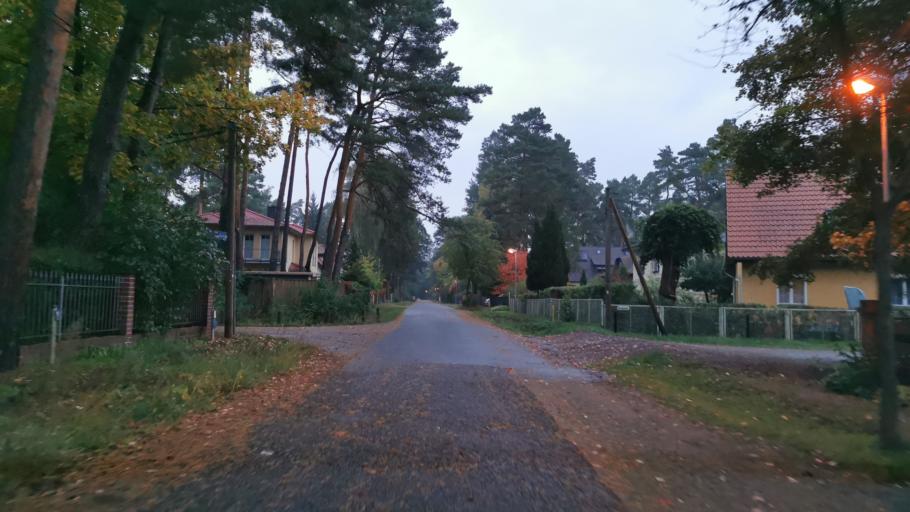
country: DE
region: Brandenburg
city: Michendorf
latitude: 52.3264
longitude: 13.0732
